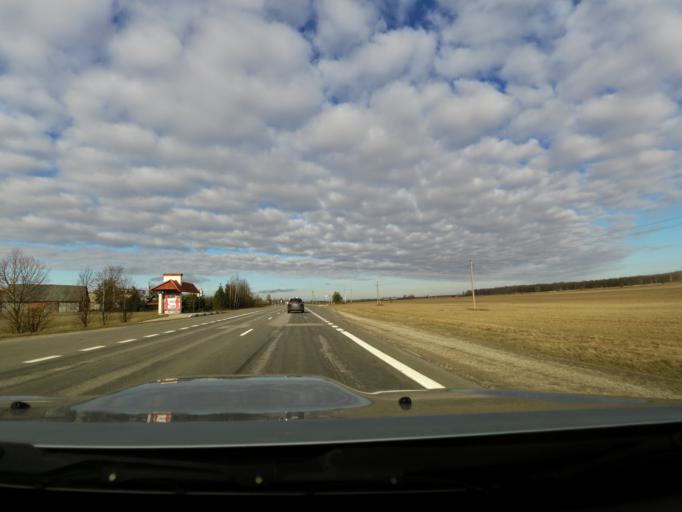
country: LT
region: Panevezys
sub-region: Panevezys City
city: Panevezys
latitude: 55.7461
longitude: 24.1631
